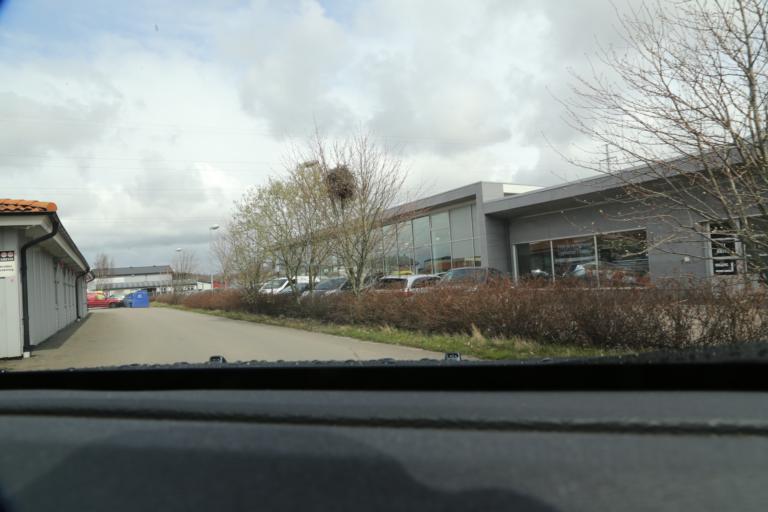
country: SE
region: Halland
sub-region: Varbergs Kommun
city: Varberg
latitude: 57.1244
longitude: 12.2955
